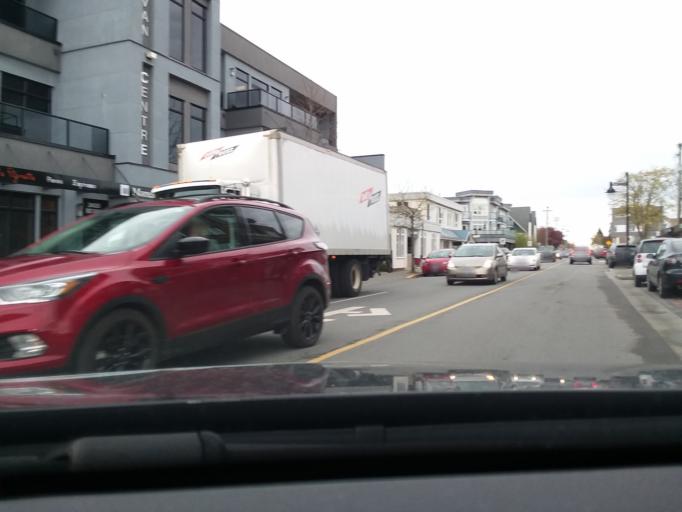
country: CA
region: British Columbia
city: North Saanich
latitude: 48.6476
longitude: -123.4001
